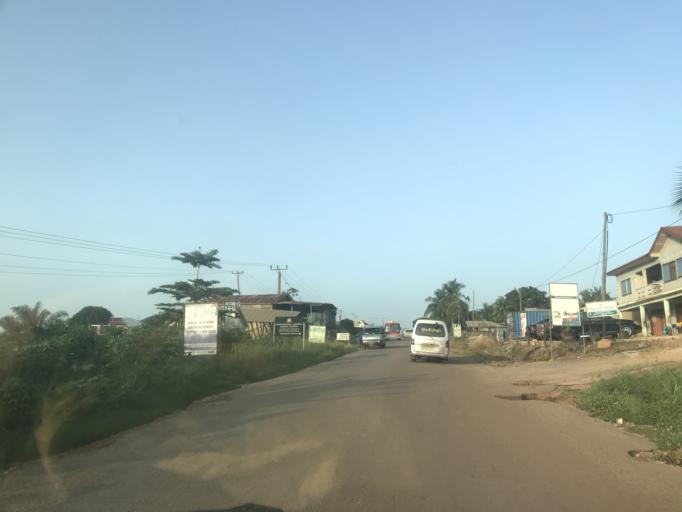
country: GH
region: Ashanti
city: Obuasi
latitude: 6.2031
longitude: -1.6076
